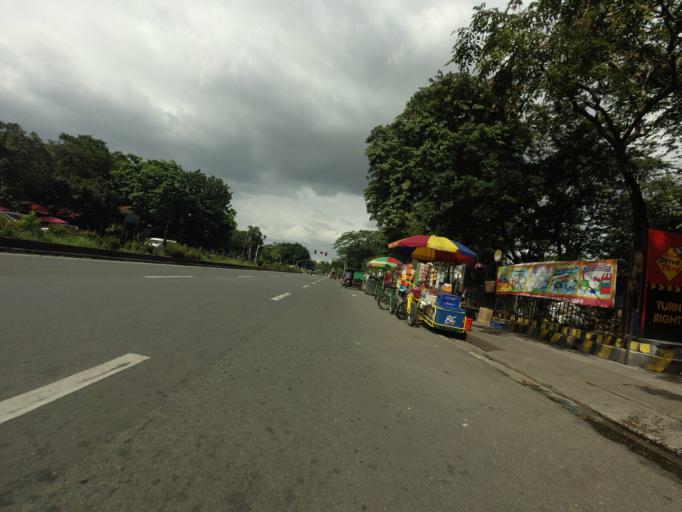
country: PH
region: Metro Manila
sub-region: City of Manila
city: Port Area
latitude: 14.5826
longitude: 120.9809
